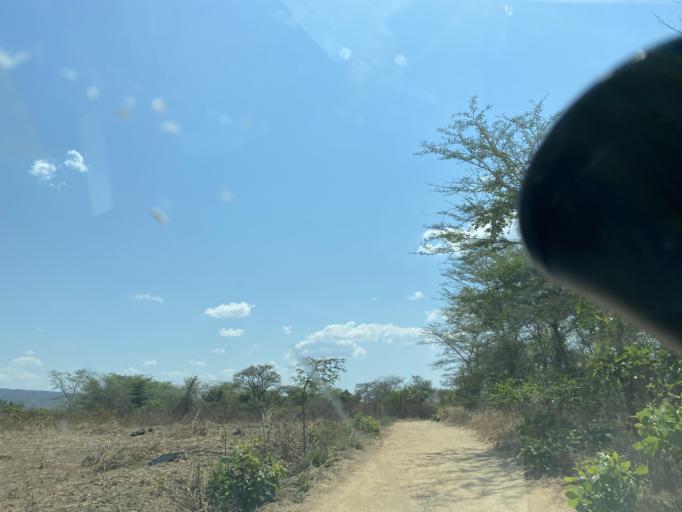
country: ZM
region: Lusaka
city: Chongwe
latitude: -15.0820
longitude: 29.5060
